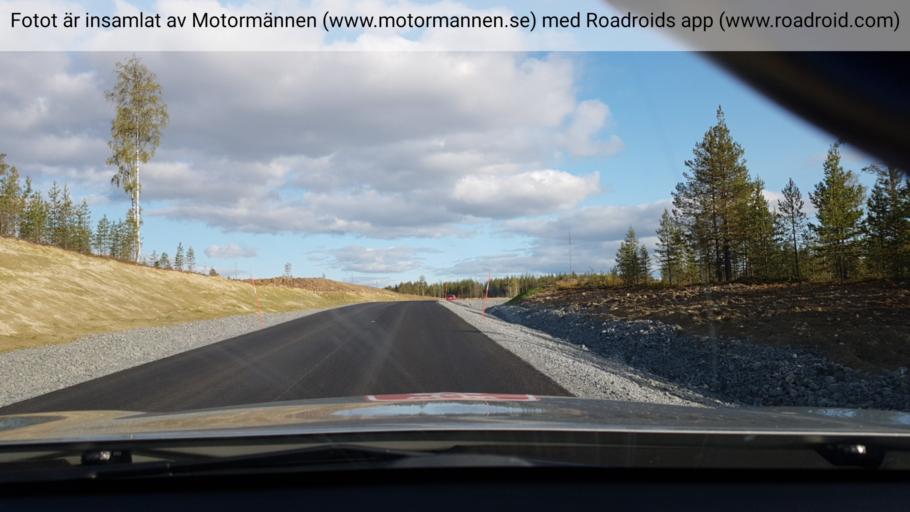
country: SE
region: Vaesterbotten
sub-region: Mala Kommun
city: Mala
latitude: 65.1673
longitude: 18.7747
